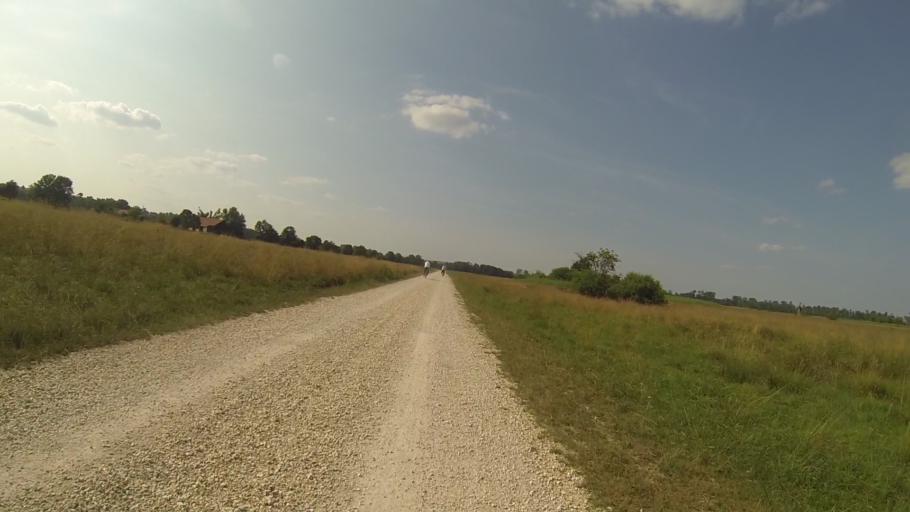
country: DE
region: Baden-Wuerttemberg
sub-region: Tuebingen Region
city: Rammingen
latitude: 48.4809
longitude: 10.1898
